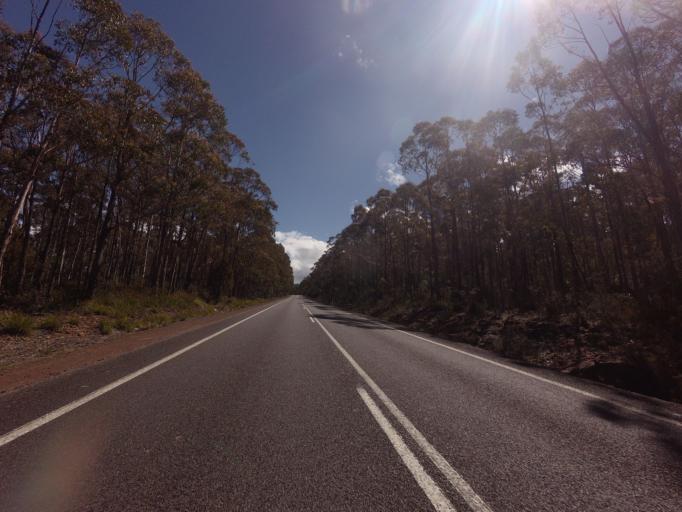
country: AU
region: Tasmania
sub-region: Northern Midlands
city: Evandale
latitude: -42.0133
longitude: 147.8667
